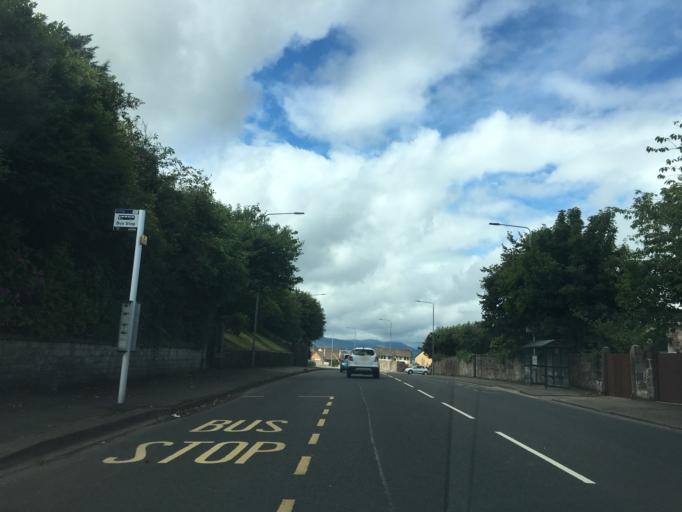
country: GB
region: Scotland
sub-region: Inverclyde
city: Gourock
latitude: 55.9619
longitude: -4.7893
